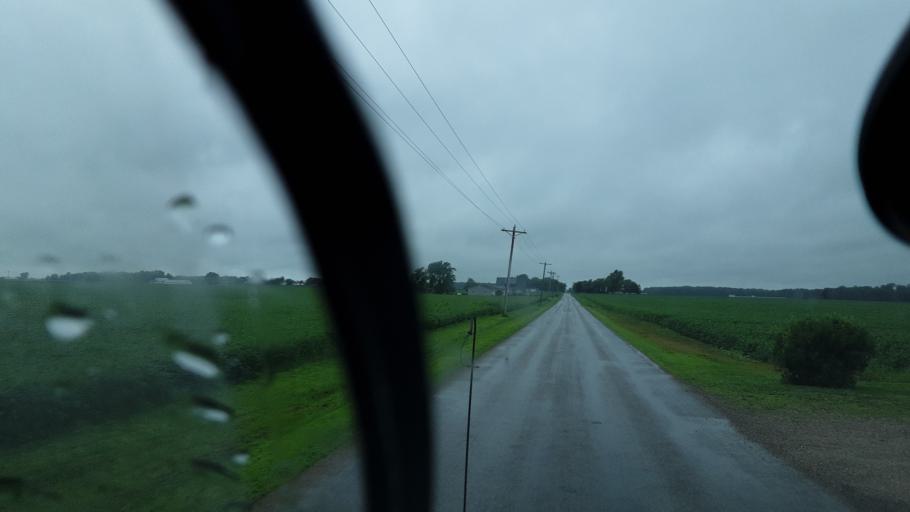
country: US
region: Indiana
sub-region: Adams County
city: Decatur
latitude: 40.7357
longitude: -84.8548
